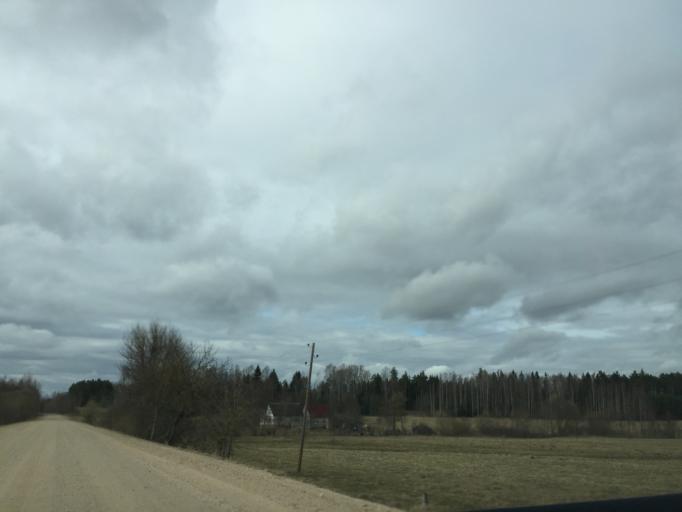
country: LV
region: Daugavpils
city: Daugavpils
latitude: 55.9543
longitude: 26.6965
